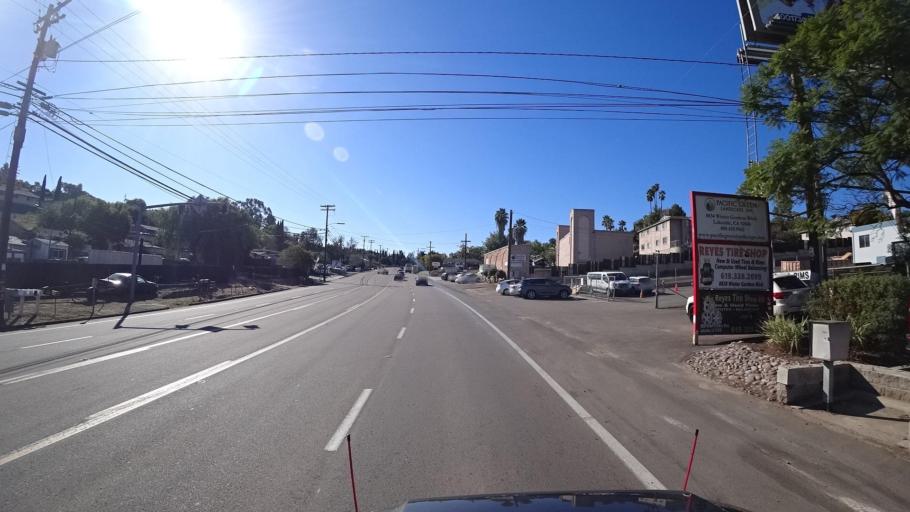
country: US
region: California
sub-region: San Diego County
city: Winter Gardens
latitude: 32.8374
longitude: -116.9336
